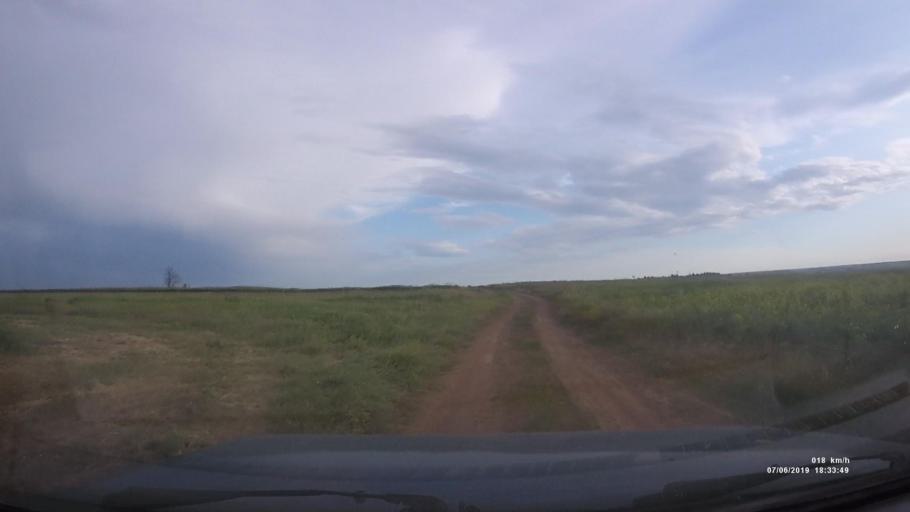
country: RU
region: Rostov
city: Staraya Stanitsa
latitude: 48.2603
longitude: 40.3624
